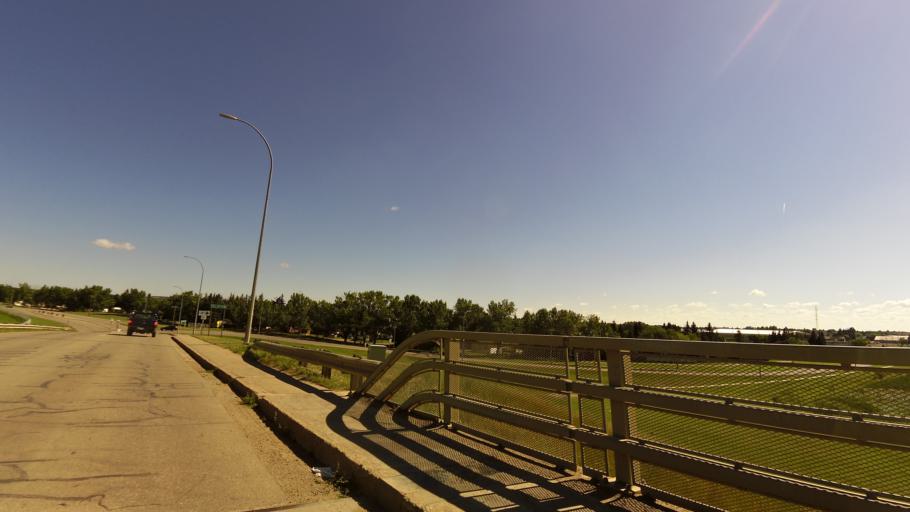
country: CA
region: Alberta
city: Wainwright
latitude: 52.8378
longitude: -110.8764
